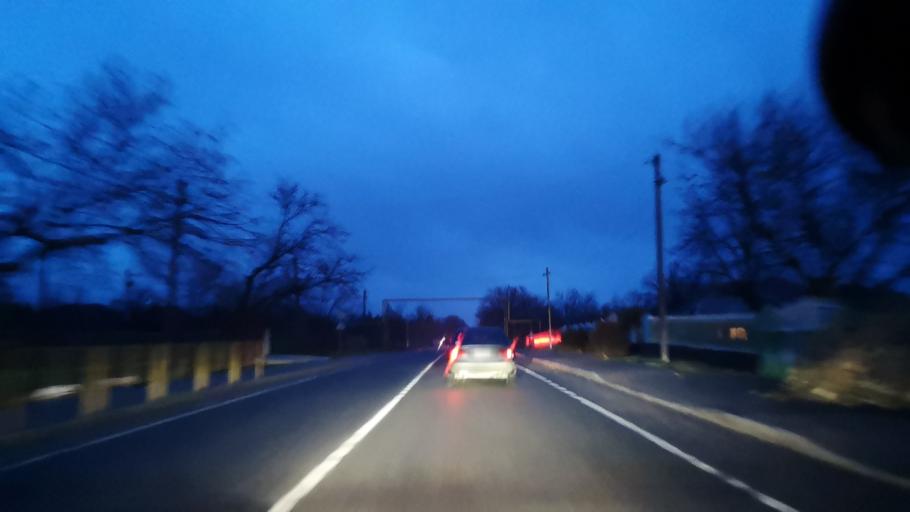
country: MD
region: Orhei
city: Orhei
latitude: 47.4353
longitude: 28.7980
